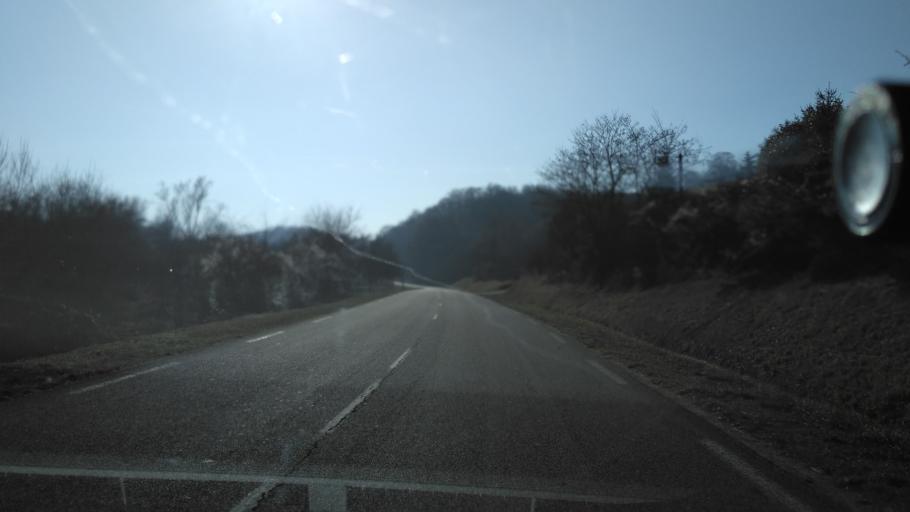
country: FR
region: Rhone-Alpes
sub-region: Departement de la Drome
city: Genissieux
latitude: 45.1280
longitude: 5.1071
